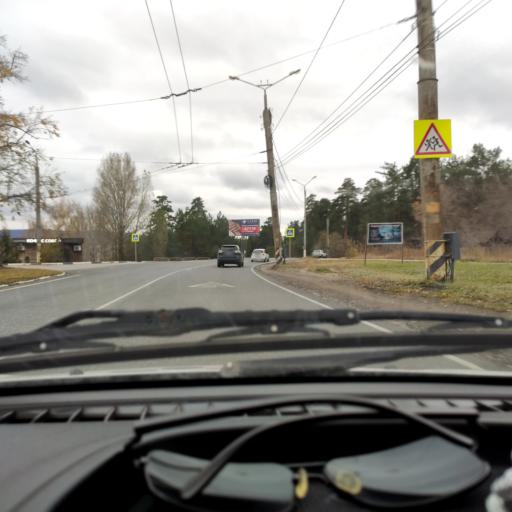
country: RU
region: Samara
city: Tol'yatti
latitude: 53.4764
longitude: 49.3489
